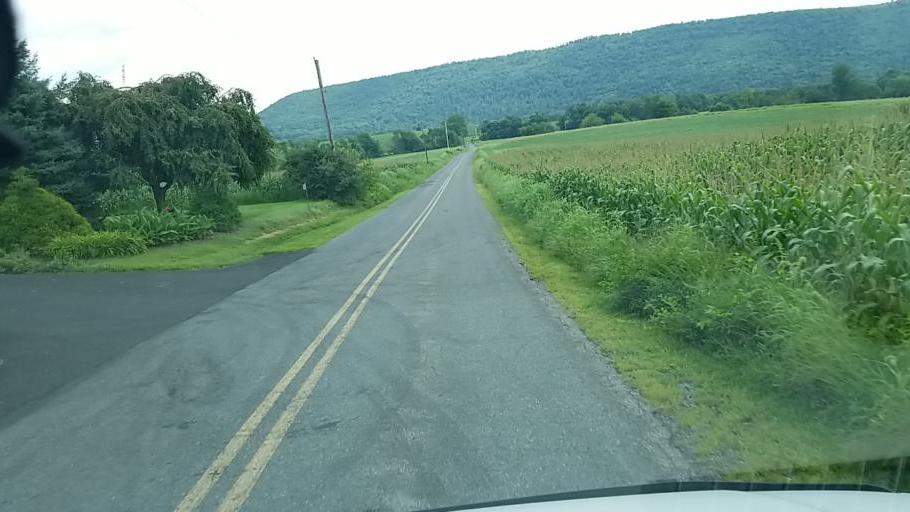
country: US
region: Pennsylvania
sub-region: Dauphin County
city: Elizabethville
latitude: 40.6470
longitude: -76.8302
